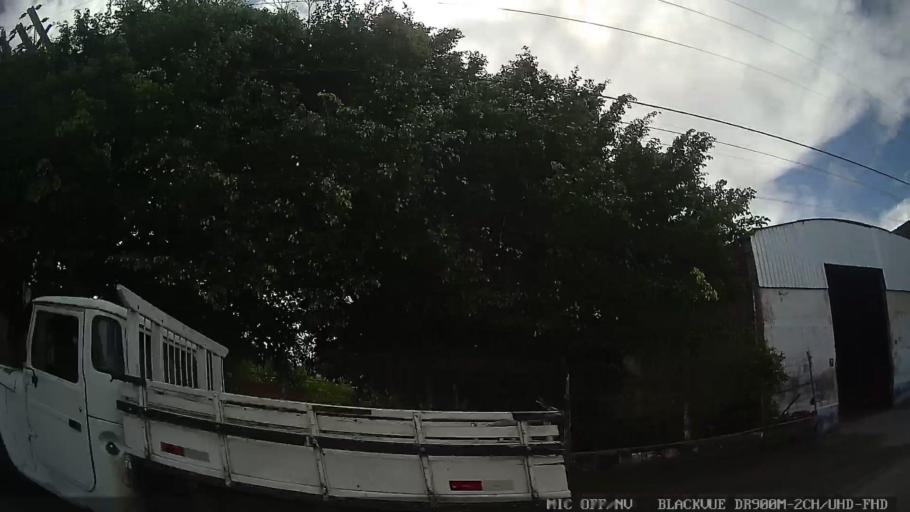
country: BR
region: Sao Paulo
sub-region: Peruibe
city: Peruibe
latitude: -24.2675
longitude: -46.9582
